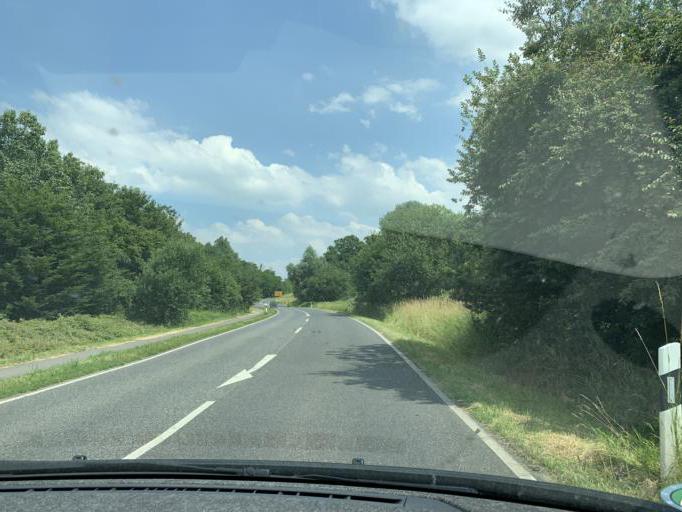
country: DE
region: North Rhine-Westphalia
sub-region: Regierungsbezirk Koln
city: Bedburg
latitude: 50.9929
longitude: 6.5816
